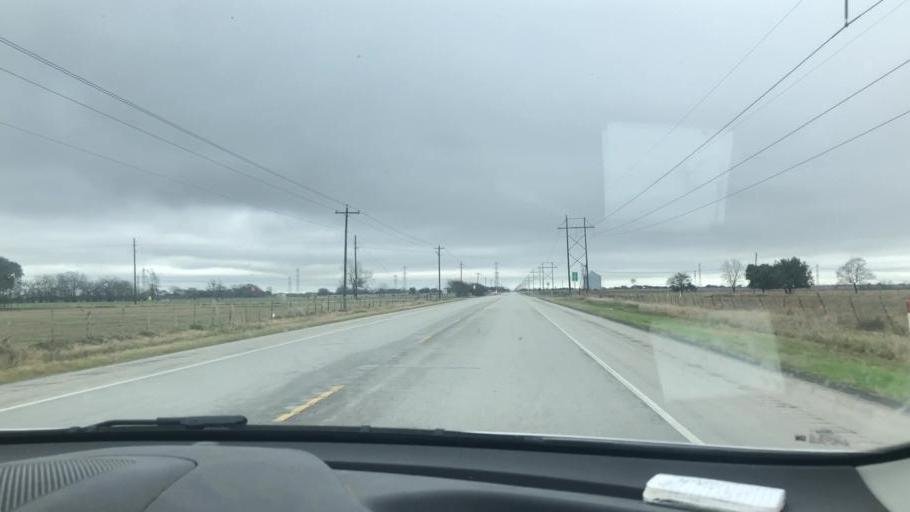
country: US
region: Texas
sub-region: Wharton County
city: Boling
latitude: 29.1847
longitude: -96.0092
